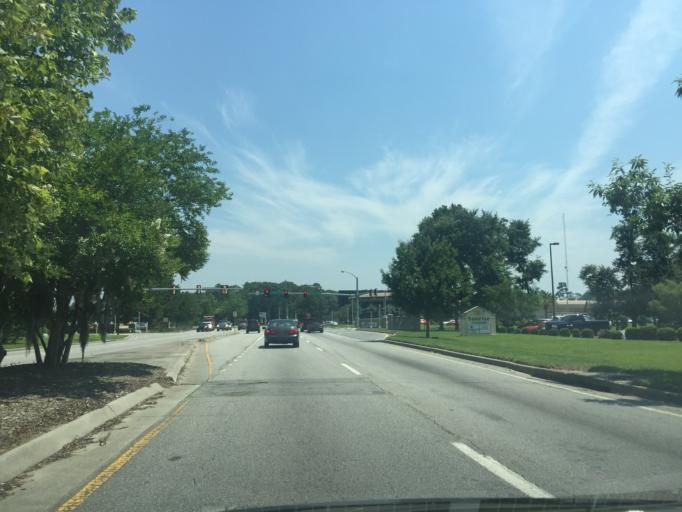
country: US
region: Georgia
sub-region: Chatham County
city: Garden City
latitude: 32.0621
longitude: -81.1601
